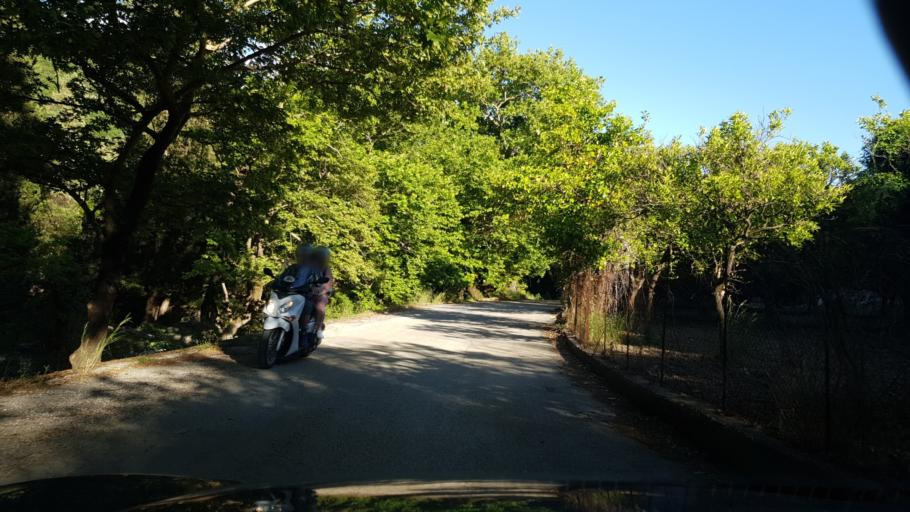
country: GR
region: Ionian Islands
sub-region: Lefkada
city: Nidri
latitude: 38.7222
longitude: 20.6935
